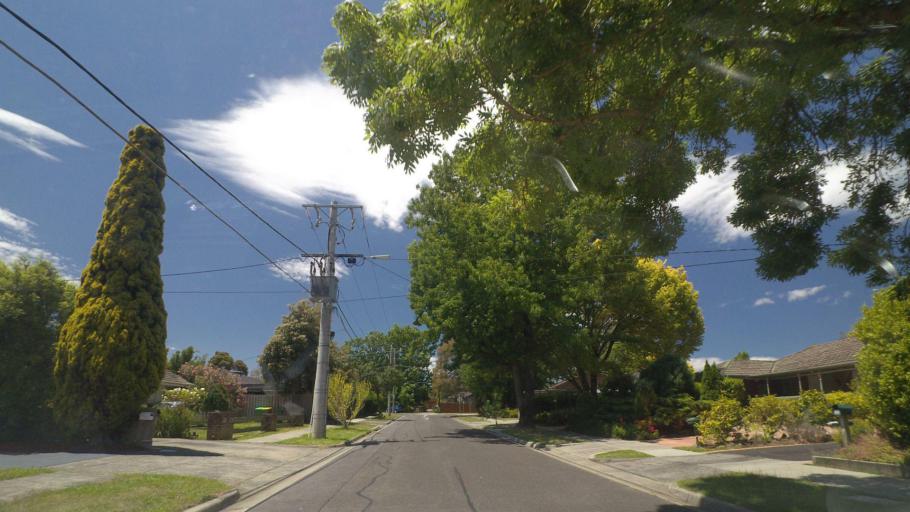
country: AU
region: Victoria
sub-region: Maroondah
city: Kilsyth South
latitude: -37.8106
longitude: 145.3200
